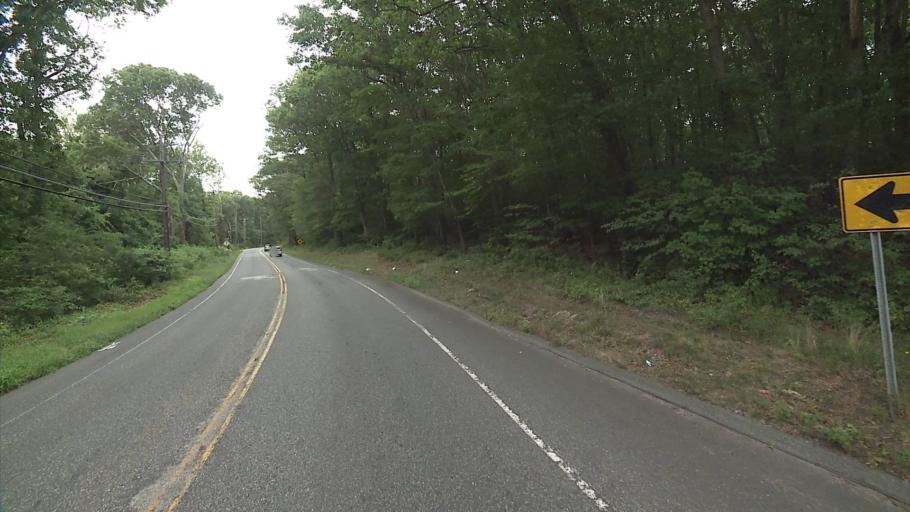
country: US
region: Connecticut
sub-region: New London County
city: Niantic
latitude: 41.3181
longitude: -72.2212
